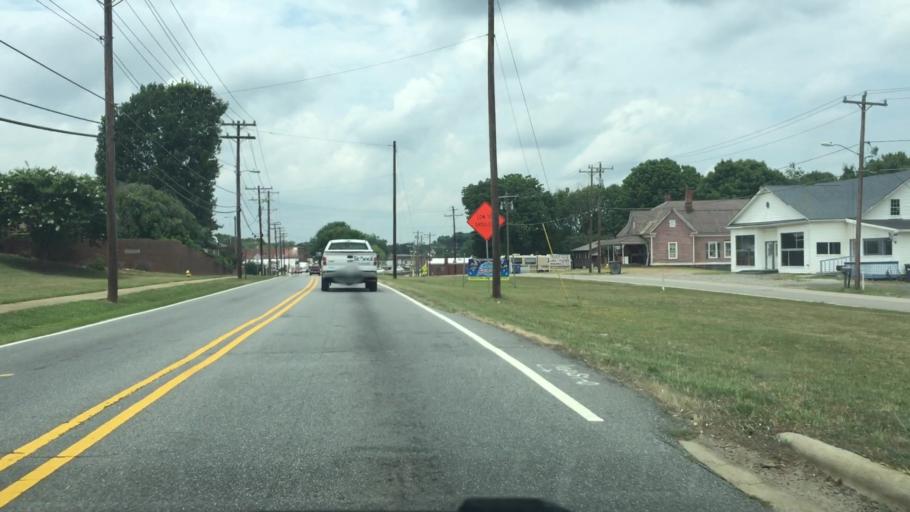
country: US
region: North Carolina
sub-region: Iredell County
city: Troutman
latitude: 35.7004
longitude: -80.8850
